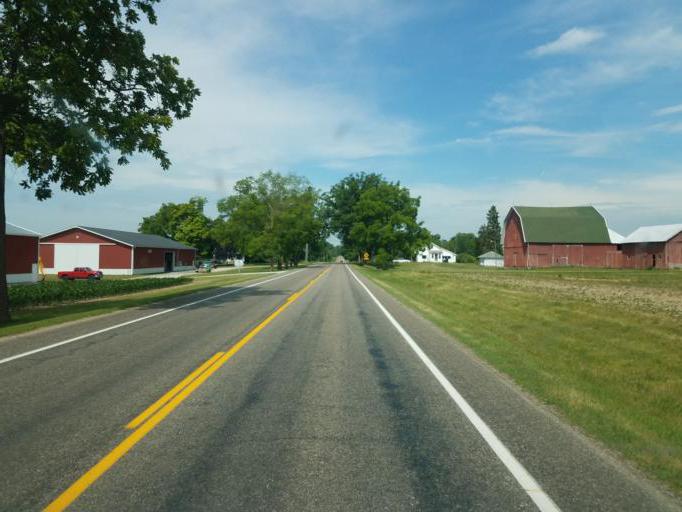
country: US
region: Michigan
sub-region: Eaton County
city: Charlotte
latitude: 42.6263
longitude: -84.9310
